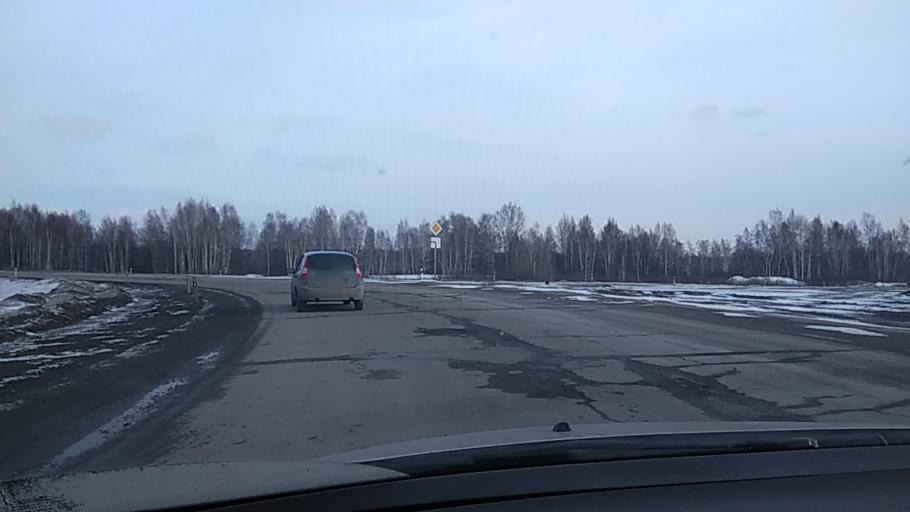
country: RU
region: Sverdlovsk
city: Pokrovskoye
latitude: 56.4608
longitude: 61.7167
